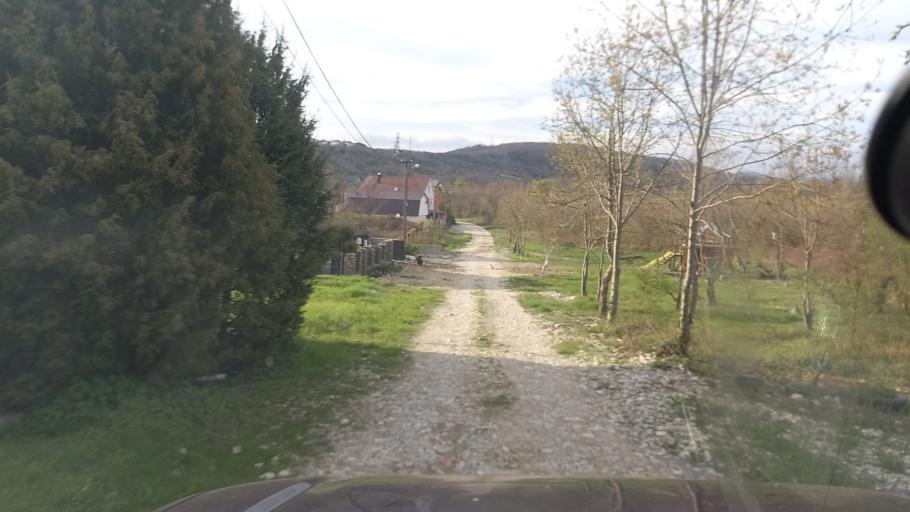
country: RU
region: Krasnodarskiy
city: Arkhipo-Osipovka
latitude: 44.3665
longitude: 38.5482
